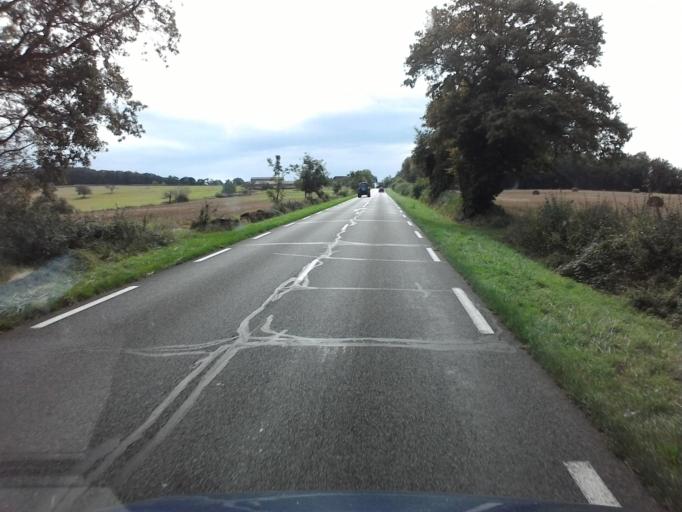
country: FR
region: Bourgogne
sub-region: Departement de Saone-et-Loire
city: Cluny
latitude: 46.5043
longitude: 4.6032
